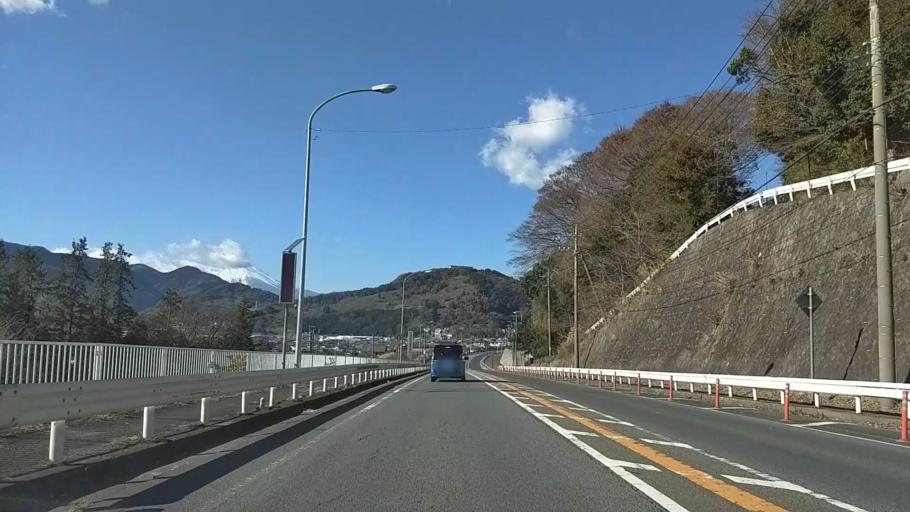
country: JP
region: Kanagawa
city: Odawara
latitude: 35.3543
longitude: 139.1144
